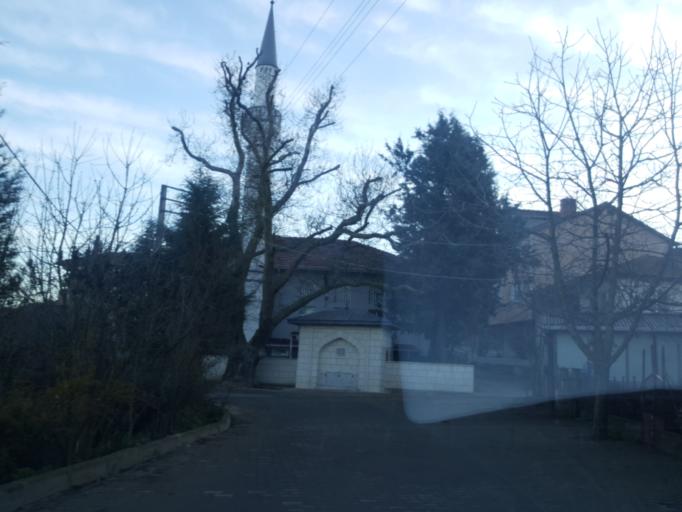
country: TR
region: Kocaeli
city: Tavsanli
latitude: 40.8459
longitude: 29.5546
